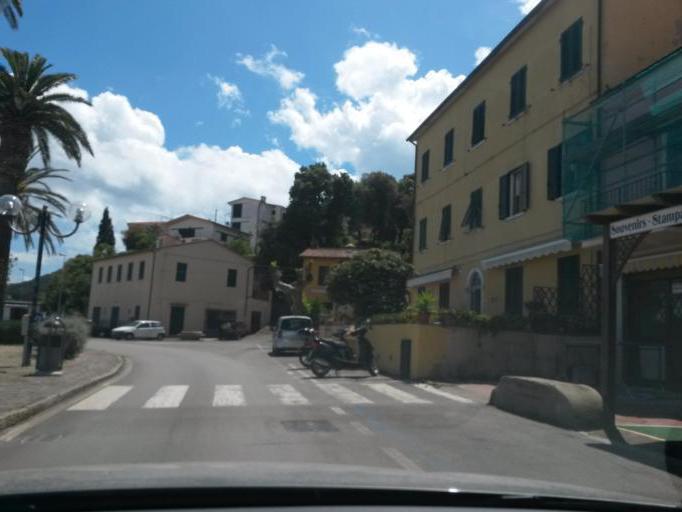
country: IT
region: Tuscany
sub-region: Provincia di Livorno
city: Rio Marina
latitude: 42.8591
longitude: 10.4218
